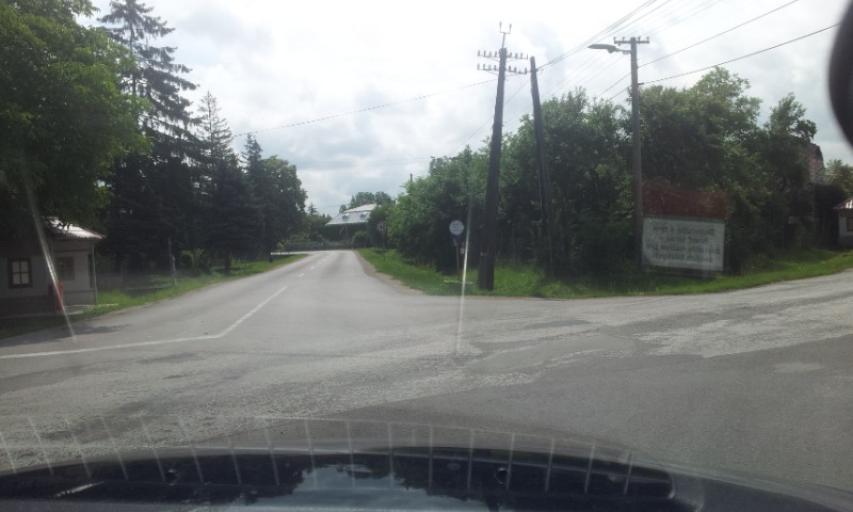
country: SK
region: Kosicky
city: Michalovce
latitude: 48.6461
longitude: 22.0004
